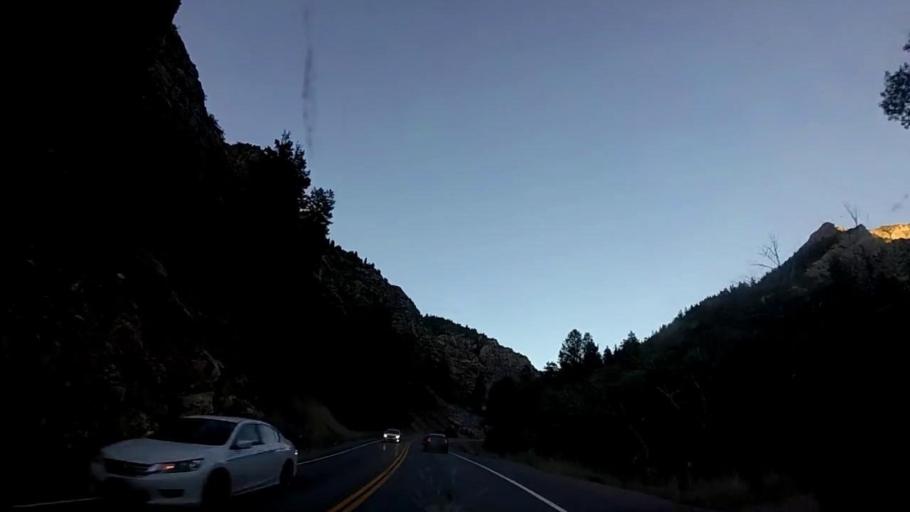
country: US
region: Utah
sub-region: Salt Lake County
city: Mount Olympus
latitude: 40.6333
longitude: -111.7191
